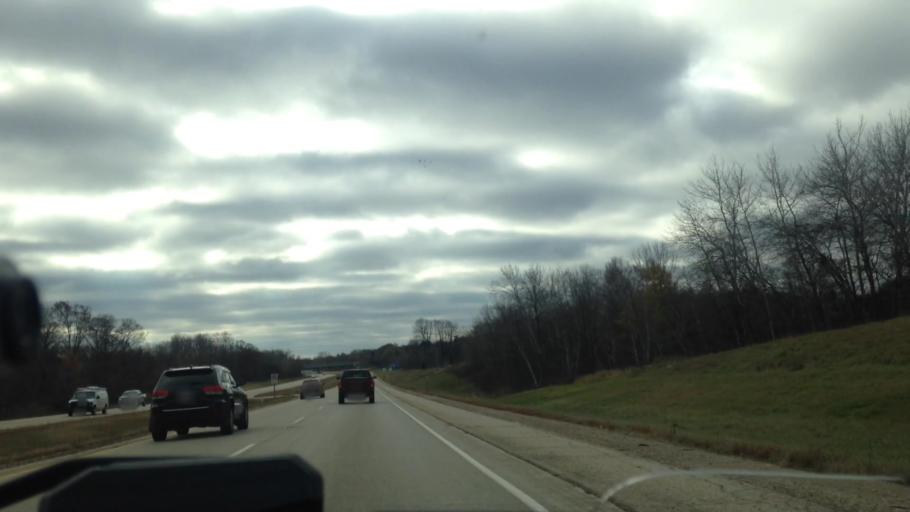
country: US
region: Wisconsin
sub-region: Washington County
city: West Bend
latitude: 43.4206
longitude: -88.2076
